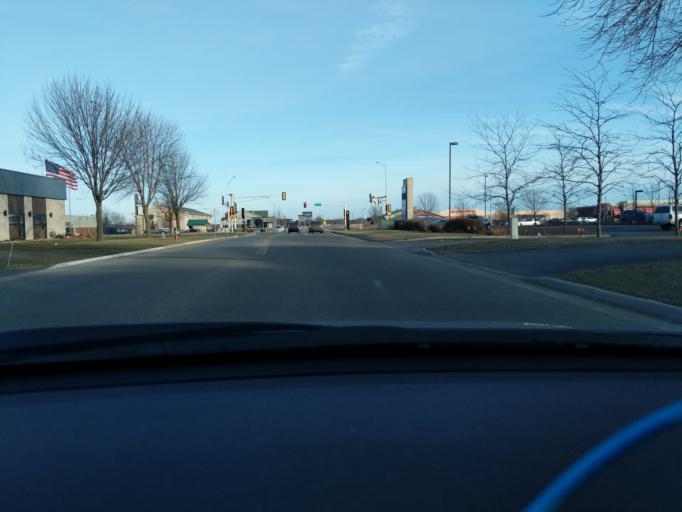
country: US
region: Minnesota
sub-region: Kandiyohi County
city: Willmar
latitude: 45.0961
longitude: -95.0440
